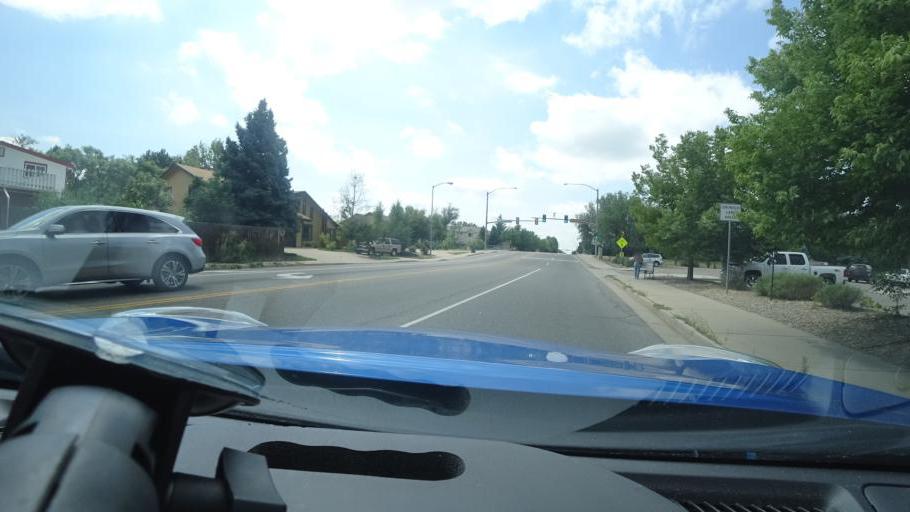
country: US
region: Colorado
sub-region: Adams County
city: Aurora
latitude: 39.7224
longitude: -104.8474
